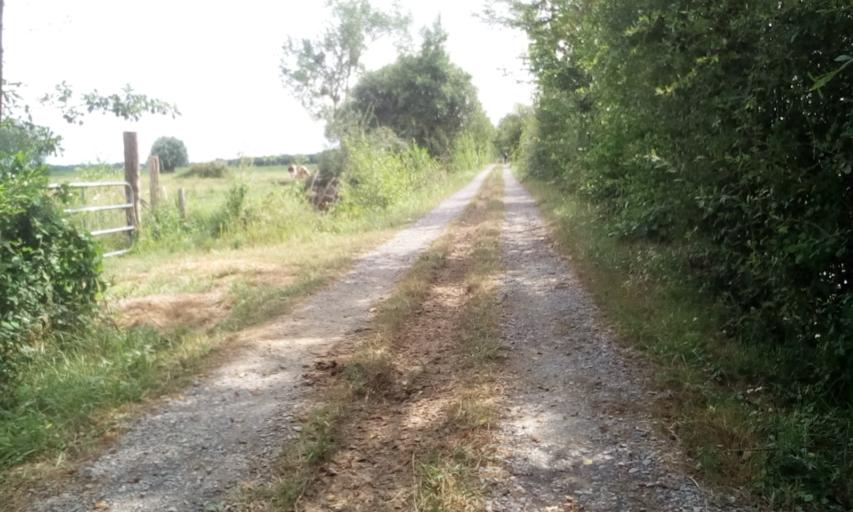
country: FR
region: Lower Normandy
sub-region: Departement du Calvados
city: Bavent
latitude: 49.2188
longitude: -0.1730
